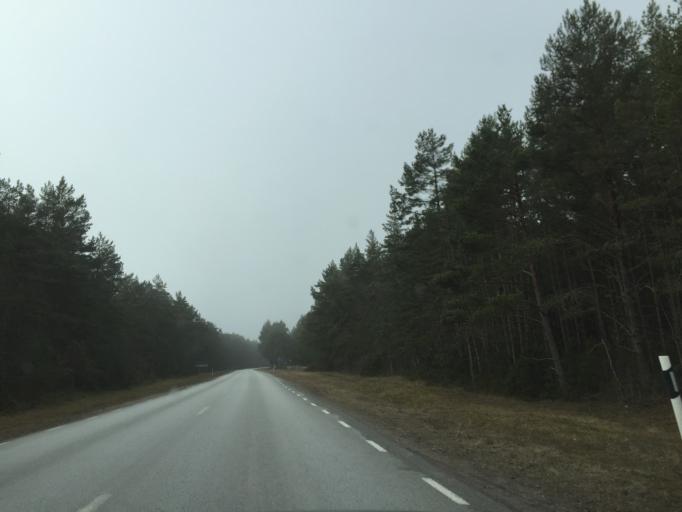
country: EE
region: Saare
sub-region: Kuressaare linn
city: Kuressaare
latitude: 58.1972
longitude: 22.2810
